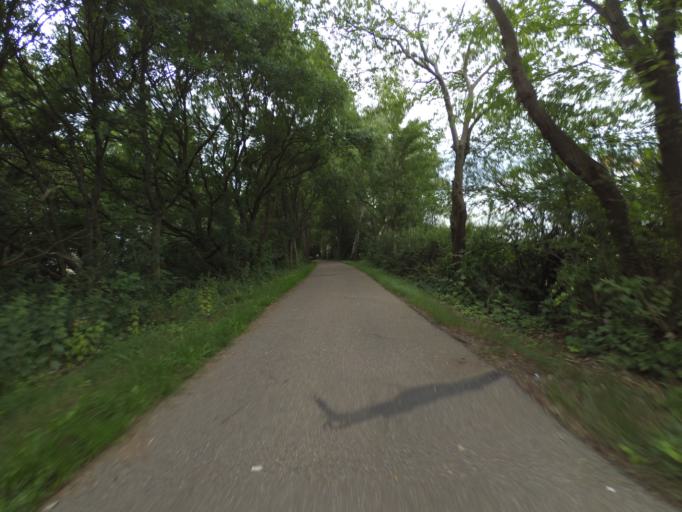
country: DE
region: North Rhine-Westphalia
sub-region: Regierungsbezirk Koln
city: Wurselen
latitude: 50.7670
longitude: 6.1656
